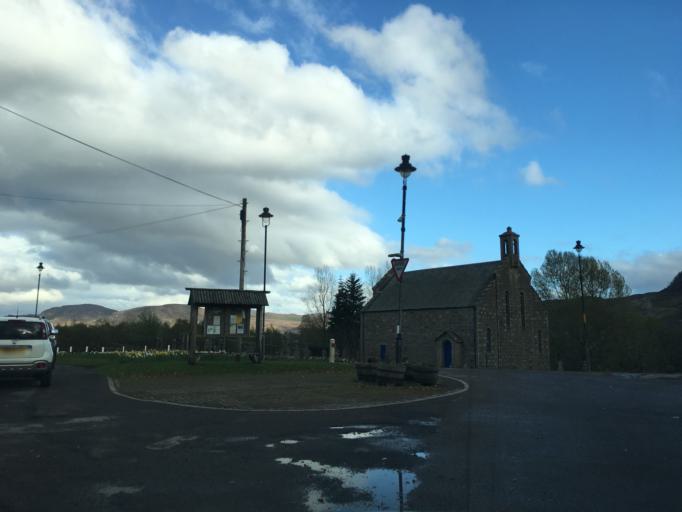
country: GB
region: Scotland
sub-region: Highland
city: Kingussie
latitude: 57.0196
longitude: -4.2835
